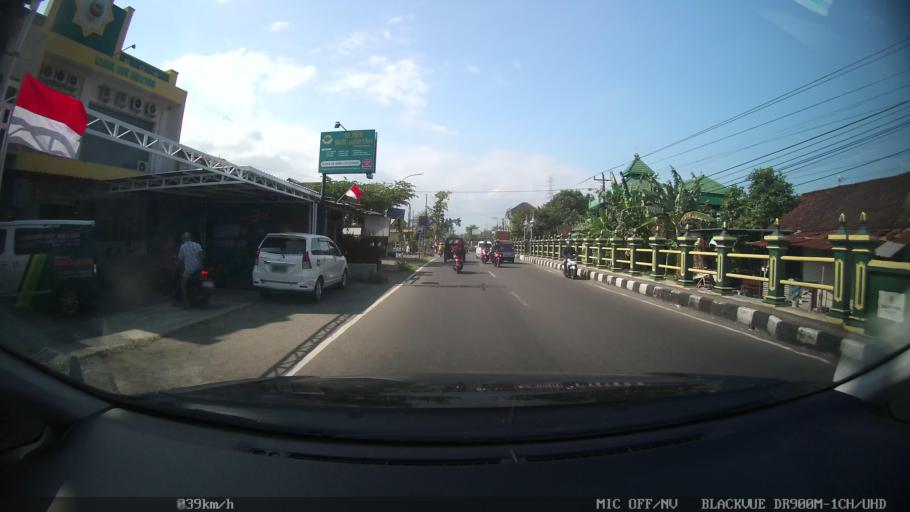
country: ID
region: Daerah Istimewa Yogyakarta
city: Sewon
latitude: -7.8876
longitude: 110.3873
